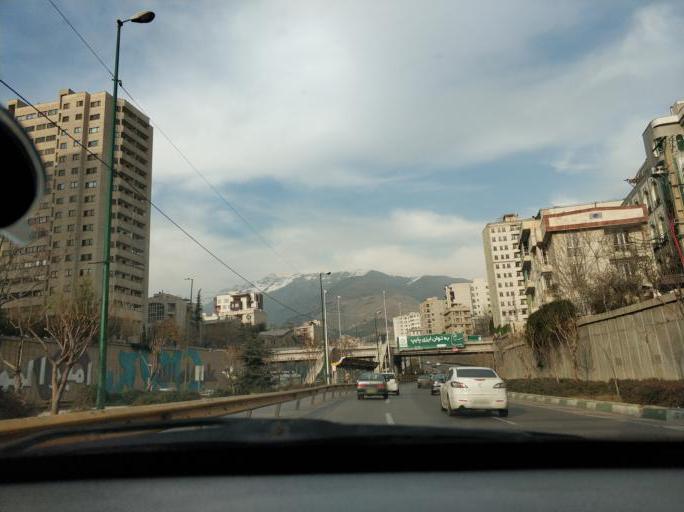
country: IR
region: Tehran
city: Tajrish
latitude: 35.7909
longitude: 51.4913
